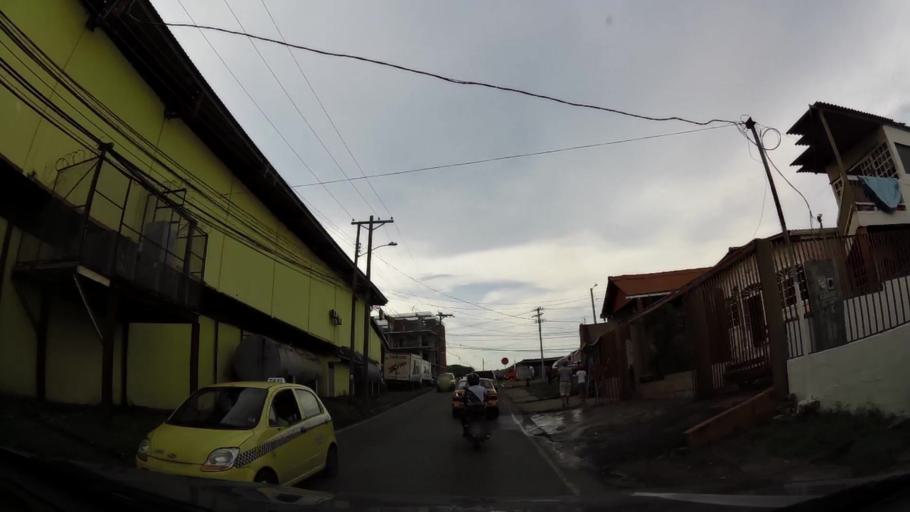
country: PA
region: Panama
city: Tocumen
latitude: 9.1044
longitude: -79.3663
